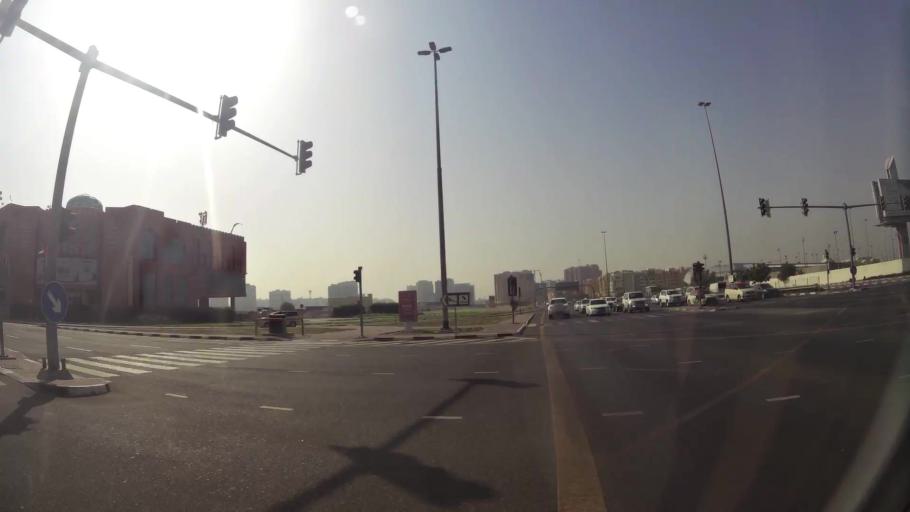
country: AE
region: Ash Shariqah
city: Sharjah
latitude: 25.2945
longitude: 55.3499
